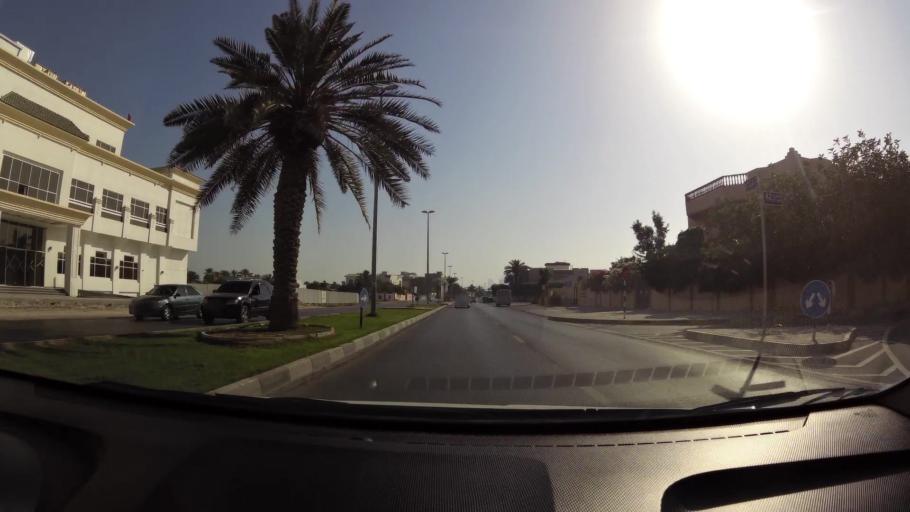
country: AE
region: Ajman
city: Ajman
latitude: 25.3821
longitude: 55.4068
